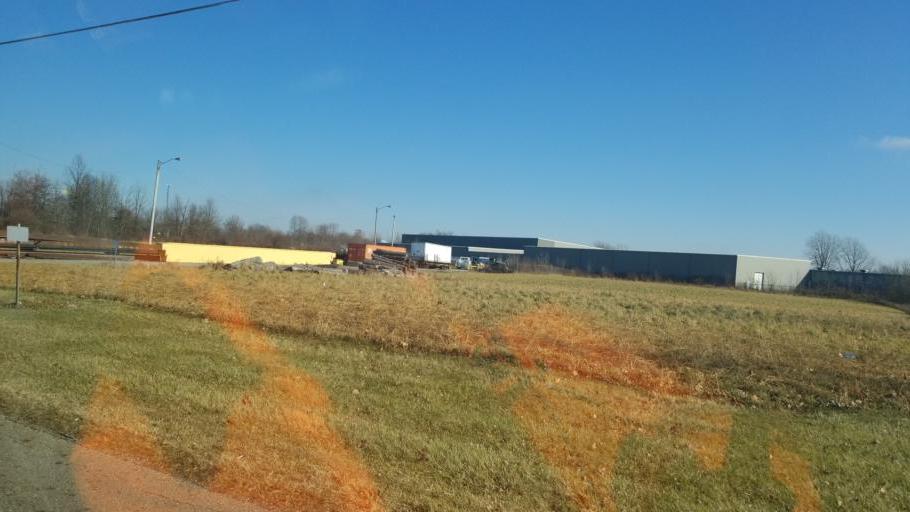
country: US
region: Ohio
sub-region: Crawford County
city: Crestline
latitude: 40.7744
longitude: -82.7480
